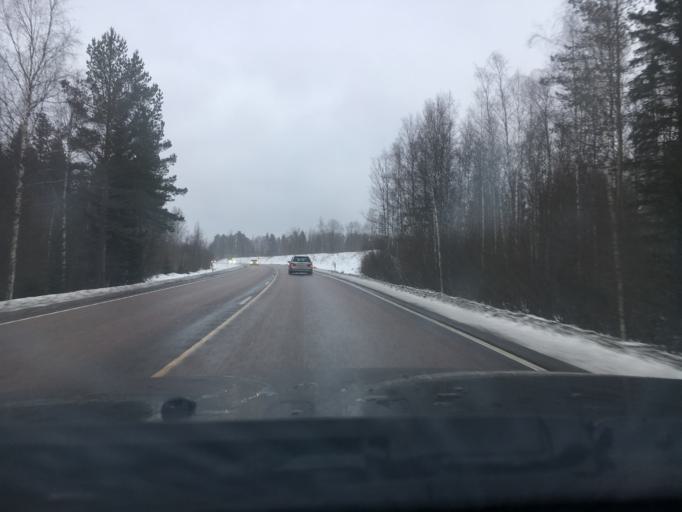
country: FI
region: Central Finland
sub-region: Joutsa
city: Joutsa
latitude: 61.7543
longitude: 26.1084
